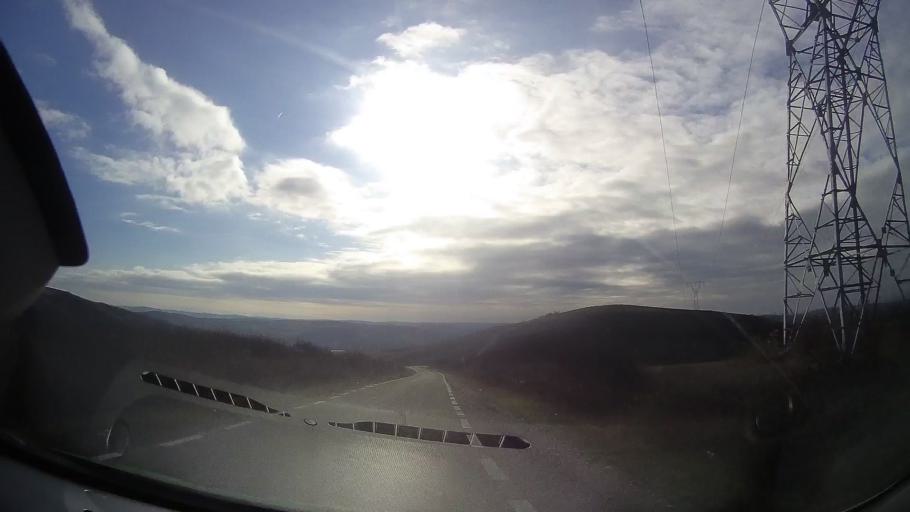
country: RO
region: Mures
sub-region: Comuna Sanger
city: Sanger
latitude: 46.5545
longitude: 24.1609
